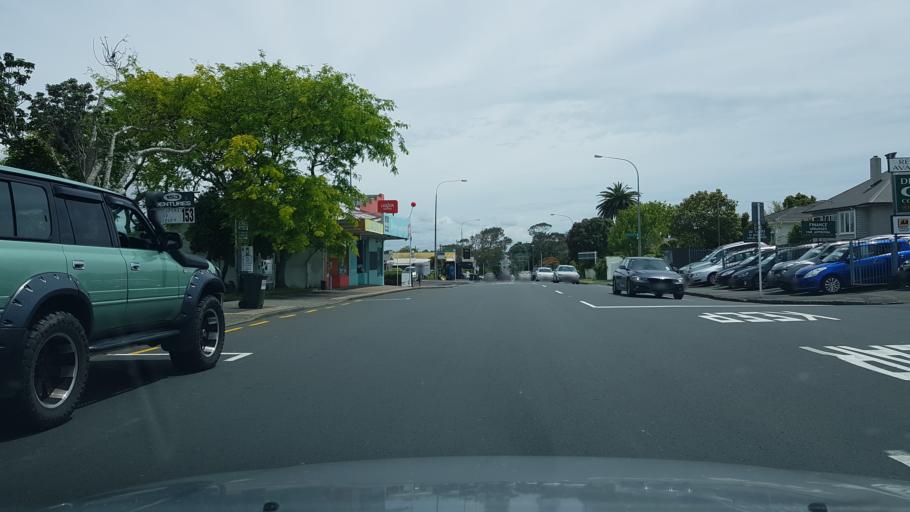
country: NZ
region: Auckland
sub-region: Auckland
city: North Shore
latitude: -36.8076
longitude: 174.7898
